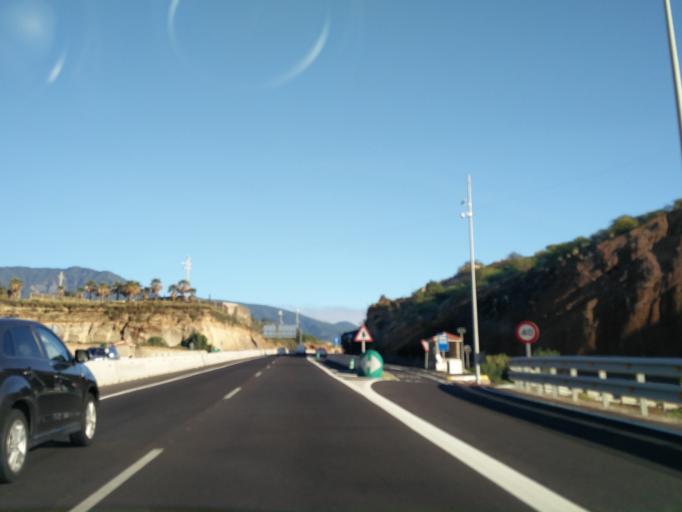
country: ES
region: Canary Islands
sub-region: Provincia de Santa Cruz de Tenerife
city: Guimar
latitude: 28.3044
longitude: -16.3832
